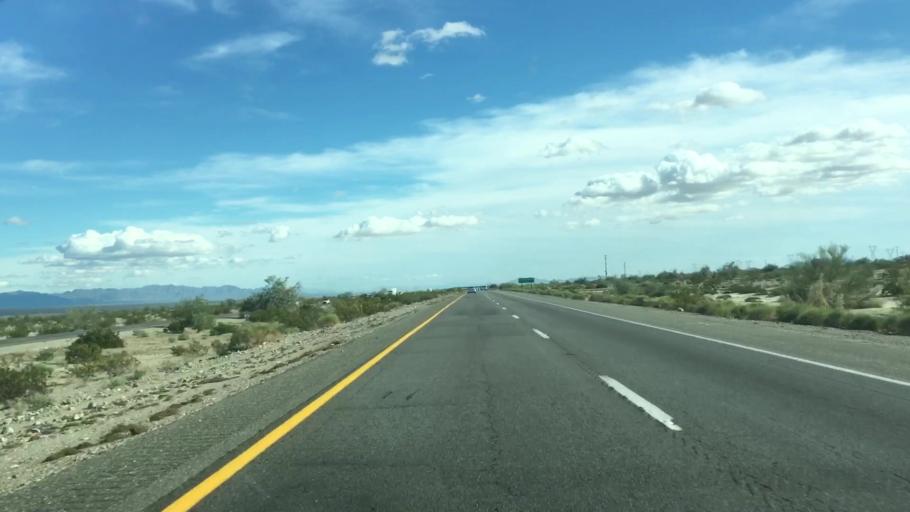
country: US
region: California
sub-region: Imperial County
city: Niland
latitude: 33.6883
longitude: -115.2637
